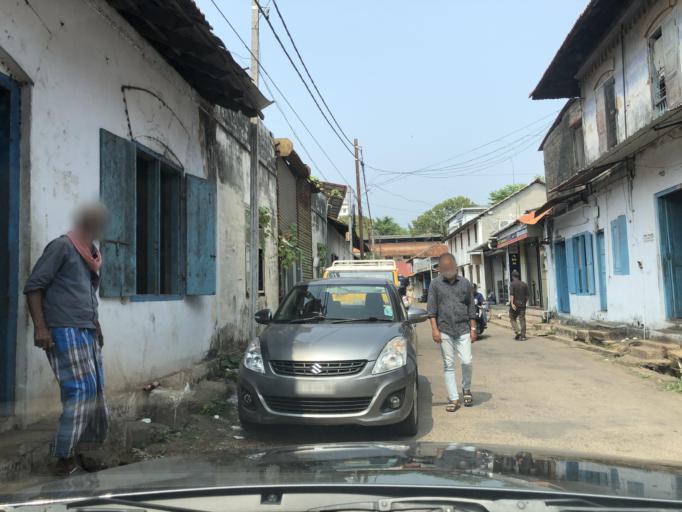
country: IN
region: Kerala
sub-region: Kozhikode
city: Kozhikode
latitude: 11.2506
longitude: 75.7755
